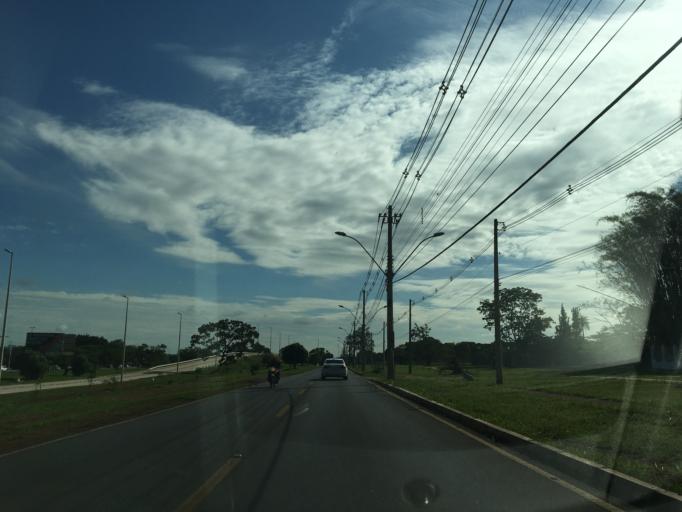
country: BR
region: Federal District
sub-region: Brasilia
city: Brasilia
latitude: -15.8718
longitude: -47.9505
